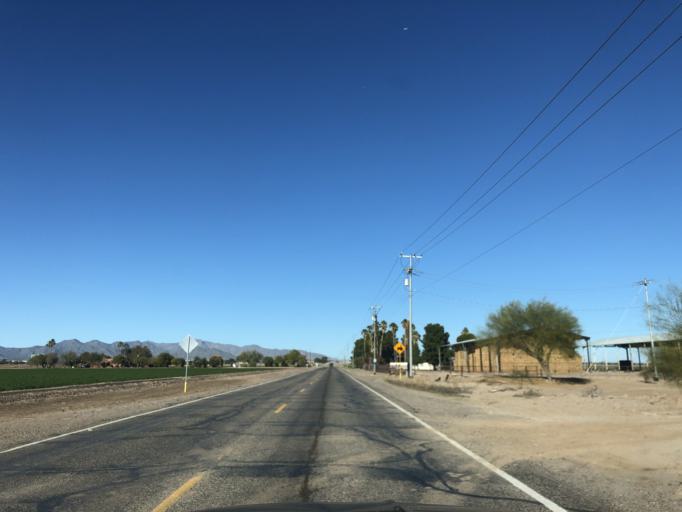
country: US
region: Arizona
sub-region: Maricopa County
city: Buckeye
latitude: 33.3804
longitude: -112.5042
